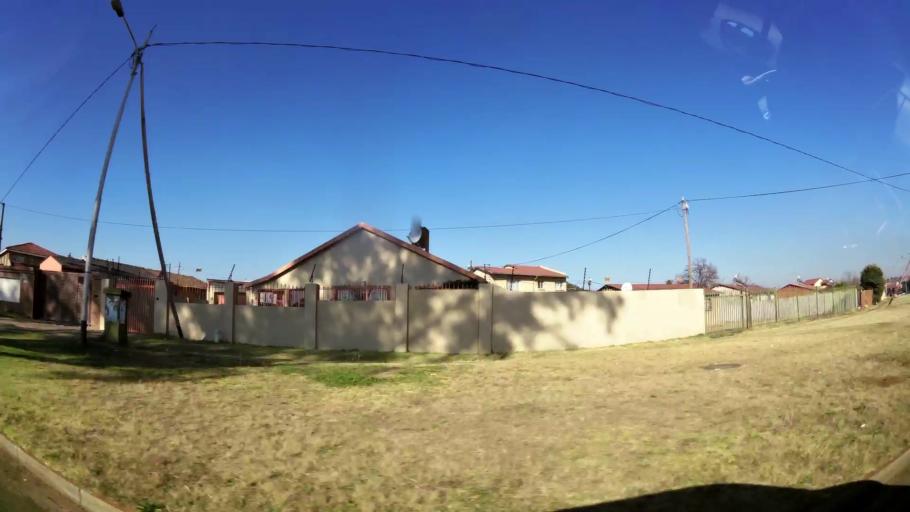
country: ZA
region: Gauteng
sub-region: City of Johannesburg Metropolitan Municipality
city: Roodepoort
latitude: -26.1539
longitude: 27.8539
